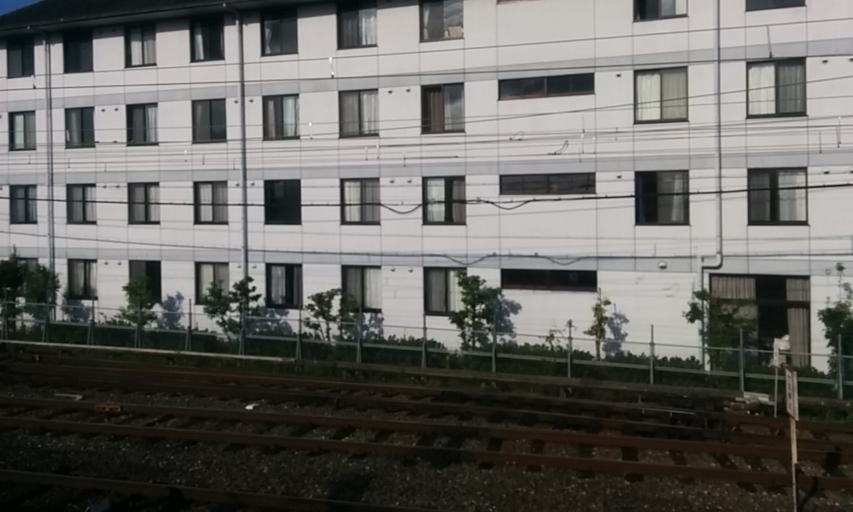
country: JP
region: Kyoto
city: Tanabe
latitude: 34.8248
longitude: 135.7735
